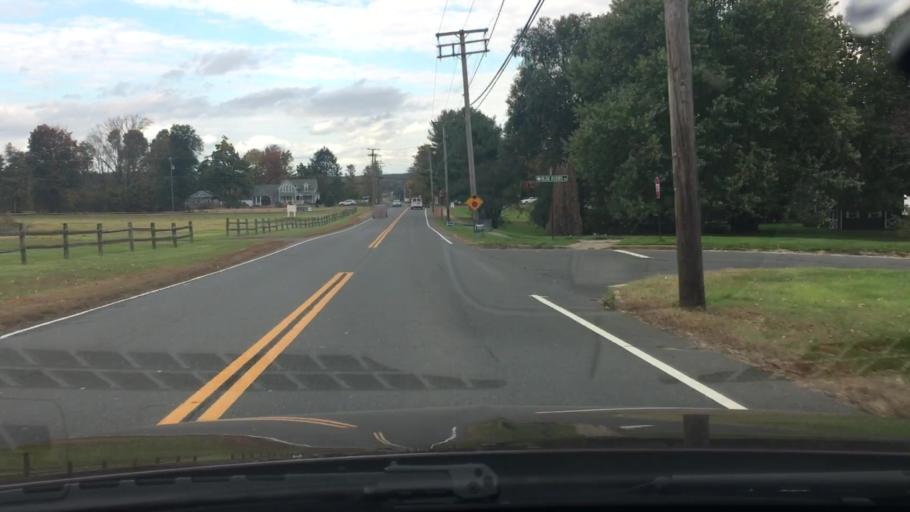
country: US
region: Connecticut
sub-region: Tolland County
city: Ellington
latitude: 41.9013
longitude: -72.4782
